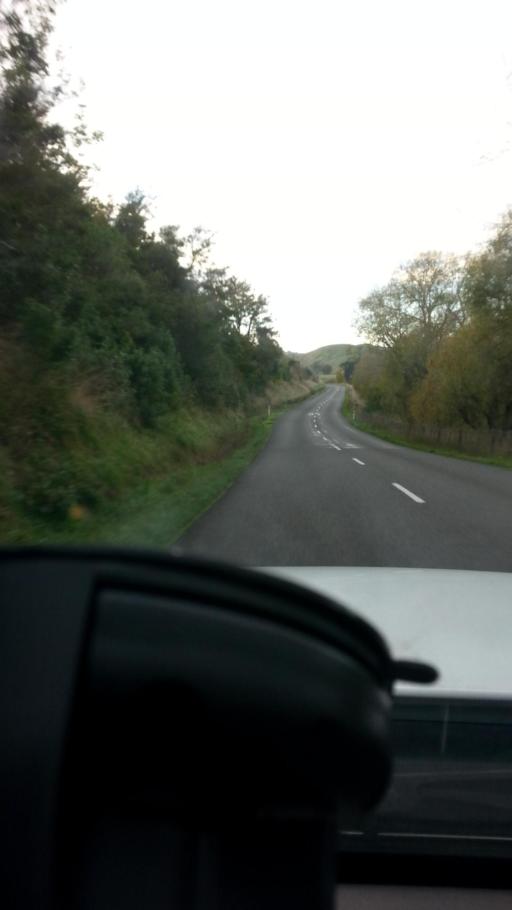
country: NZ
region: Wellington
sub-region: Masterton District
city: Masterton
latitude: -40.9691
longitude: 175.7820
